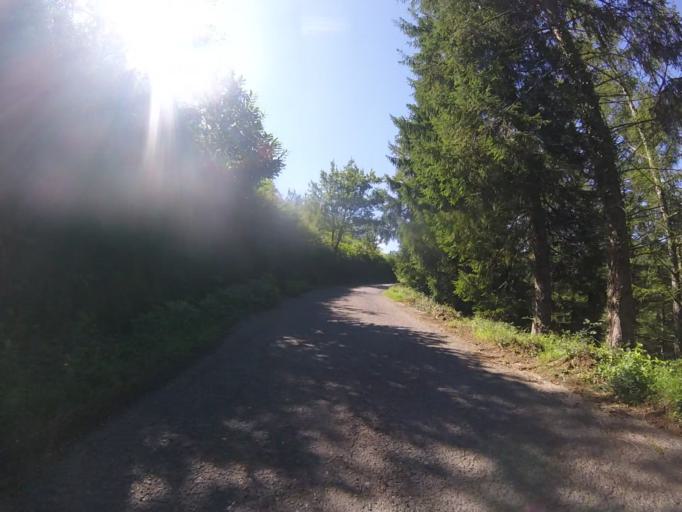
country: ES
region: Navarre
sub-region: Provincia de Navarra
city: Goizueta
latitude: 43.1847
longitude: -1.8278
